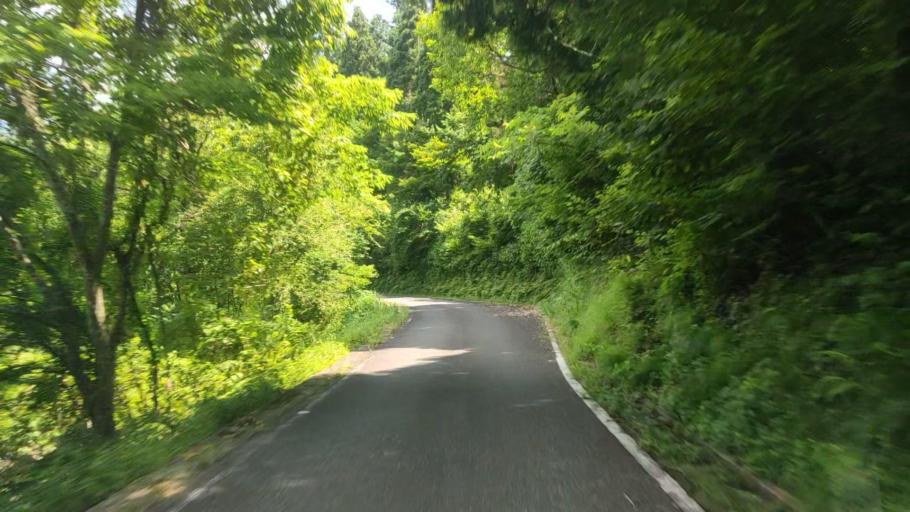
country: JP
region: Fukui
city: Ono
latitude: 35.7548
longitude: 136.5738
